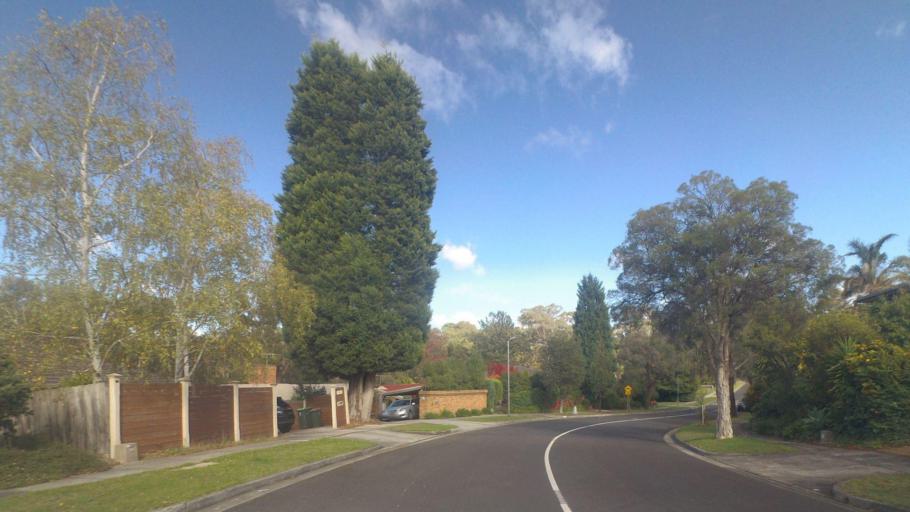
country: AU
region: Victoria
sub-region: Whitehorse
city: Vermont
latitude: -37.8453
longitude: 145.1923
